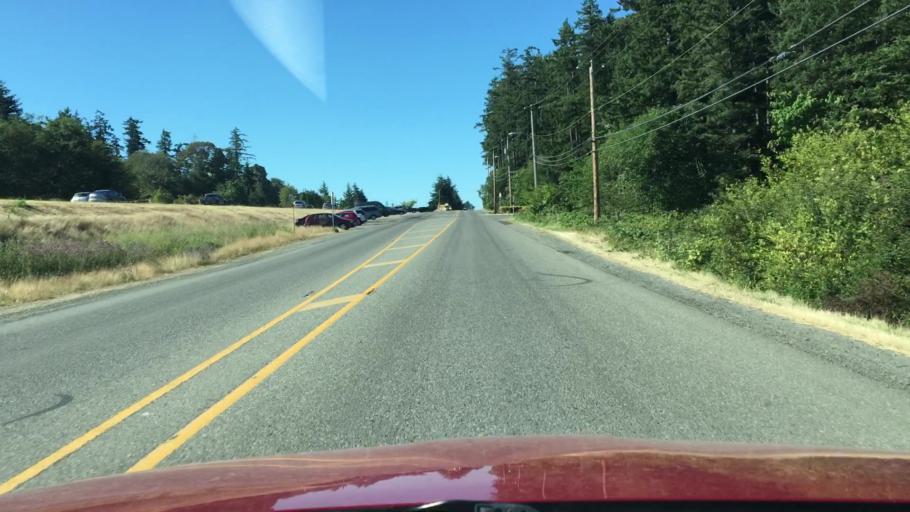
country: CA
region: British Columbia
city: Victoria
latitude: 48.5100
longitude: -123.3846
